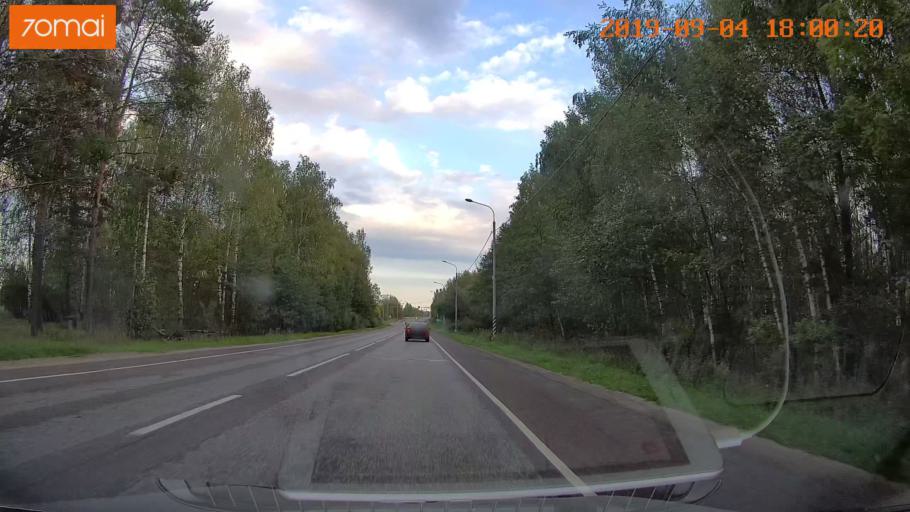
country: RU
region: Moskovskaya
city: Il'inskiy Pogost
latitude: 55.4912
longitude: 38.8599
